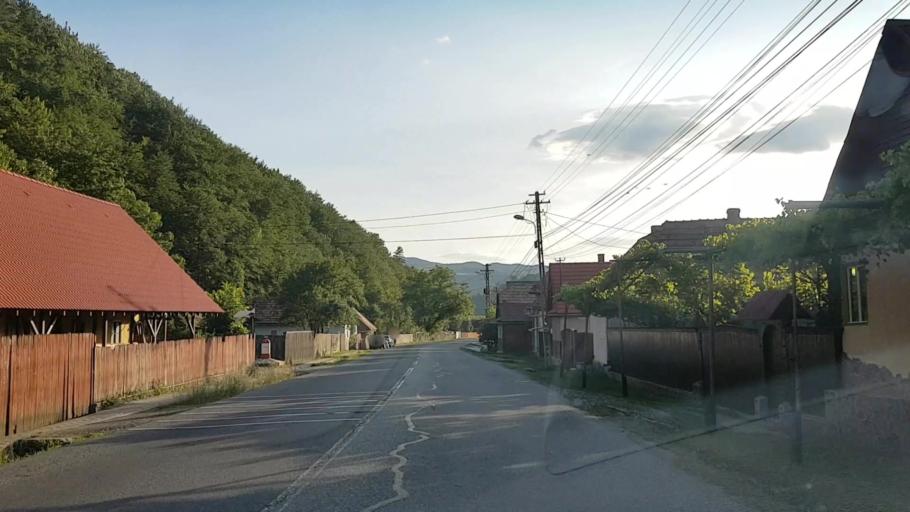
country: RO
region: Harghita
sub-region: Comuna Praid
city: Praid
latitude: 46.5608
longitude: 25.1428
